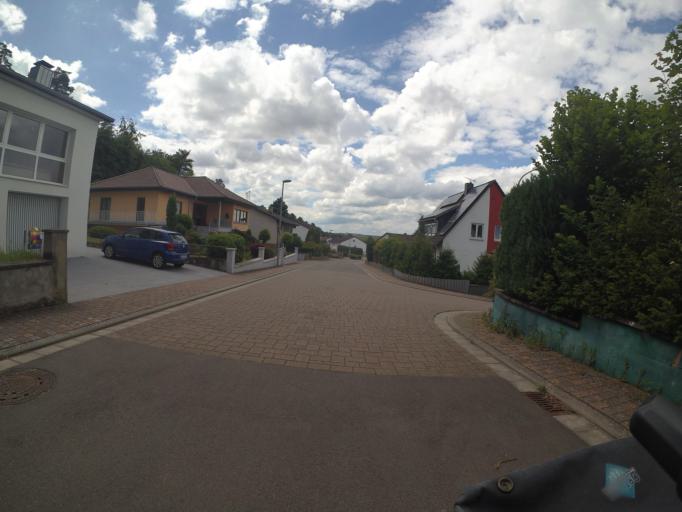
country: DE
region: Rheinland-Pfalz
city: Rodenbach
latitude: 49.4689
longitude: 7.6674
